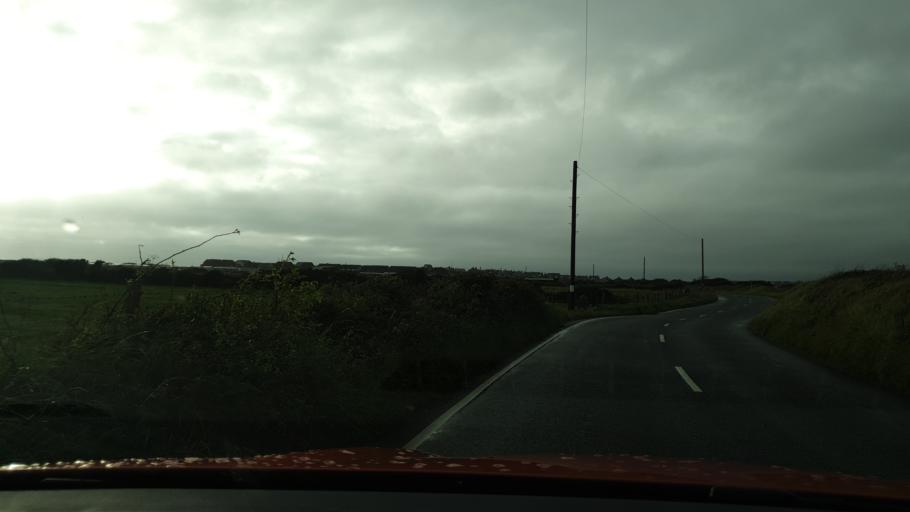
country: GB
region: England
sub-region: Cumbria
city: Barrow in Furness
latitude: 54.0914
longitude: -3.2471
